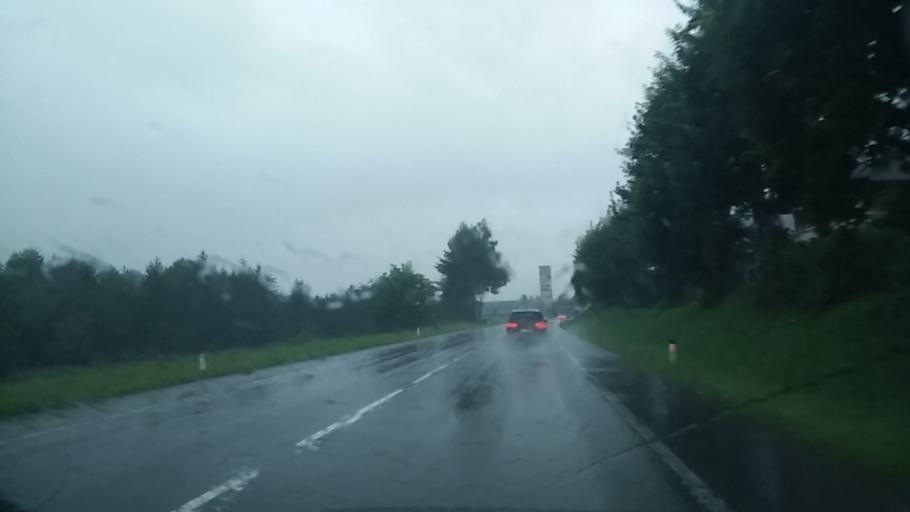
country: AT
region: Carinthia
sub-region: Politischer Bezirk Villach Land
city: Wernberg
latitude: 46.6197
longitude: 13.9483
